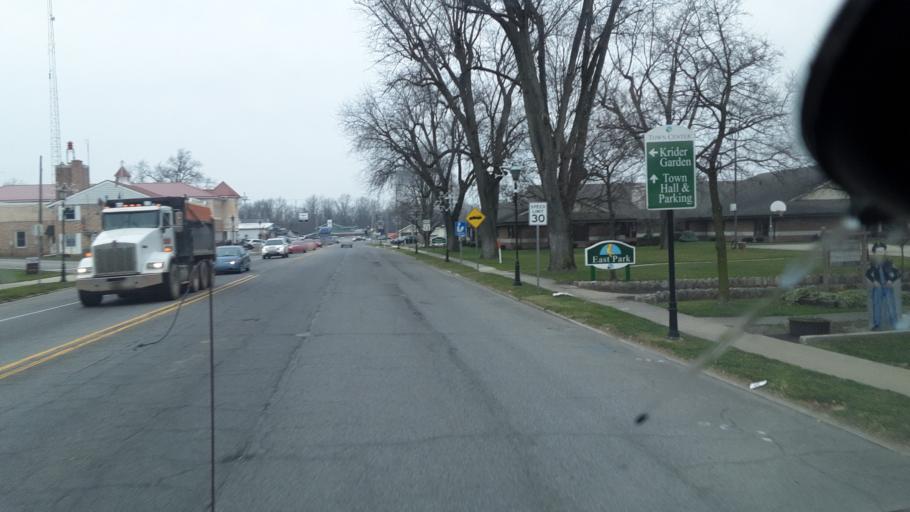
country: US
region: Indiana
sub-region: Elkhart County
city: Middlebury
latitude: 41.6756
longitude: -85.7060
